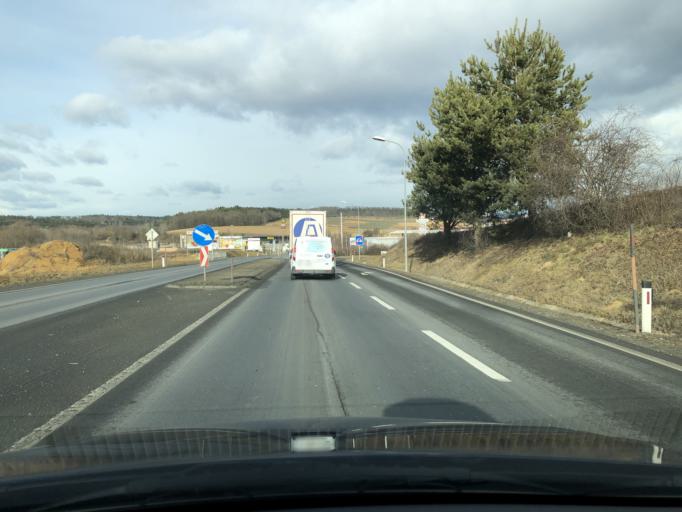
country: AT
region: Burgenland
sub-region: Politischer Bezirk Oberwart
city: Oberwart
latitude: 47.2818
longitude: 16.1890
